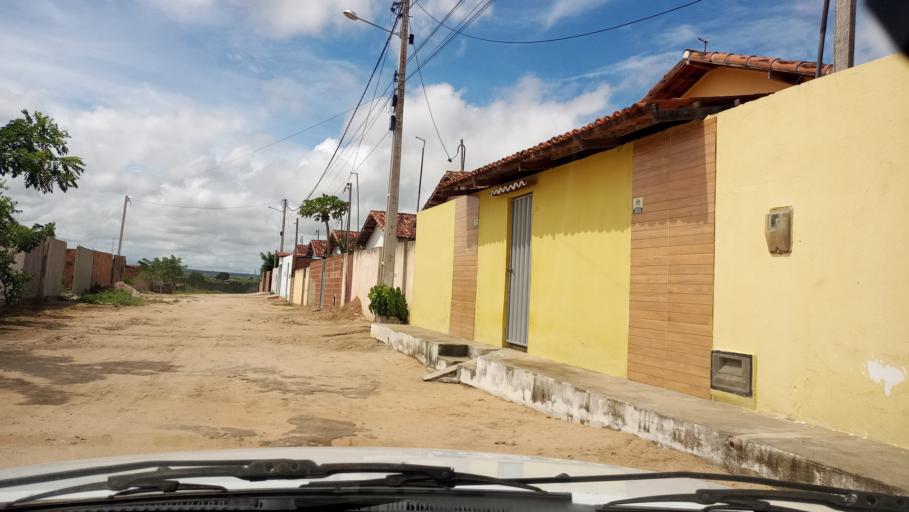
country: BR
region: Rio Grande do Norte
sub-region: Brejinho
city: Brejinho
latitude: -6.1577
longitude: -35.4413
